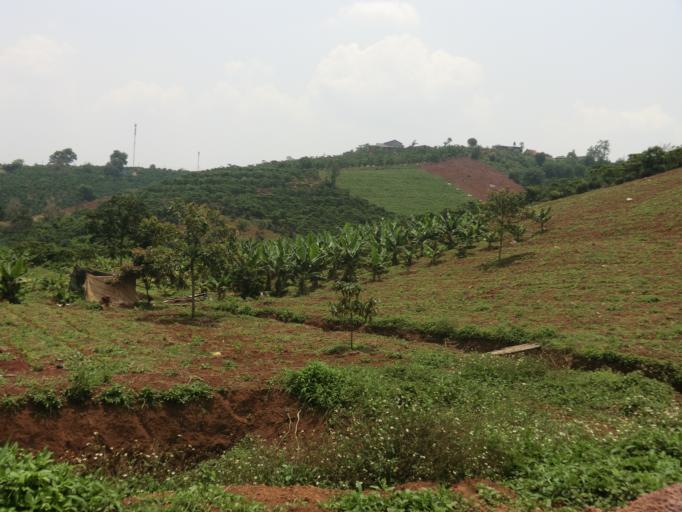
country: VN
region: Lam Dong
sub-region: Thanh Pho Bao Loc
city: Bao Loc
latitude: 11.5906
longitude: 107.7886
